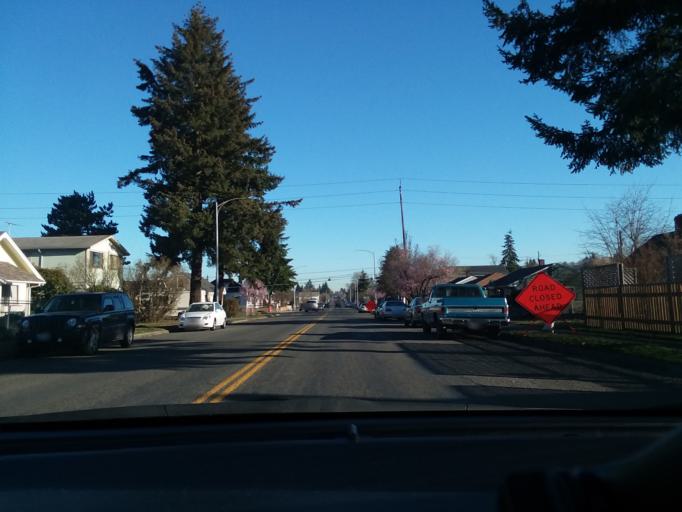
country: US
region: Washington
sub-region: Pierce County
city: Lakewood
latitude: 47.1965
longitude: -122.4723
